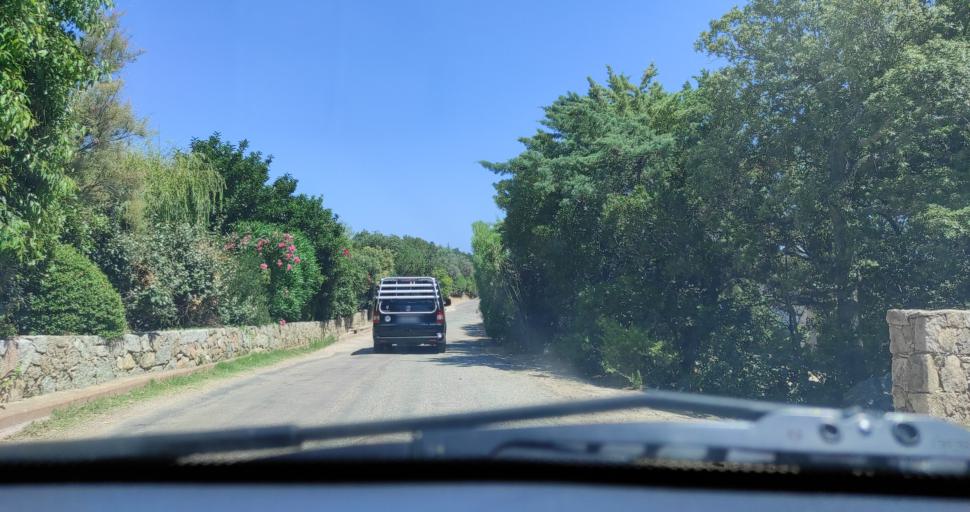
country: FR
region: Corsica
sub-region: Departement de la Corse-du-Sud
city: Porto-Vecchio
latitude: 41.6198
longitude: 9.3498
